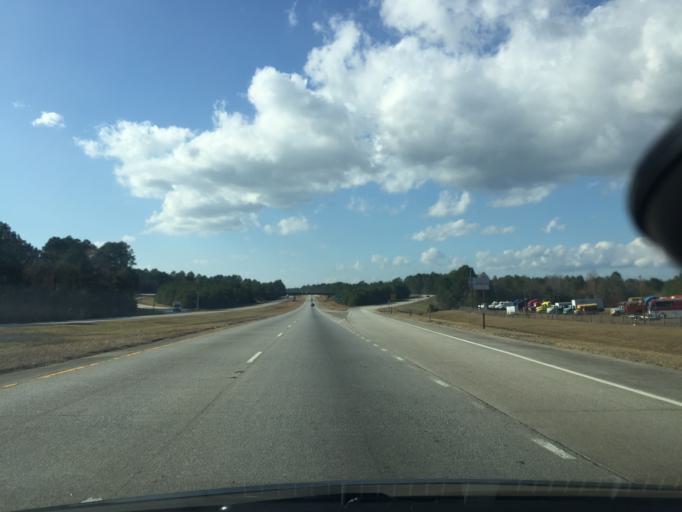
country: US
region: Georgia
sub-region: Emanuel County
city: Swainsboro
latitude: 32.4171
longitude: -82.3868
